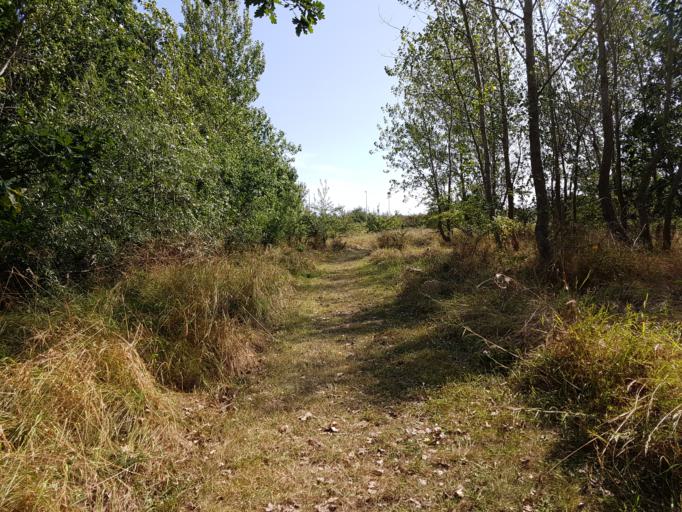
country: DK
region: Zealand
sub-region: Guldborgsund Kommune
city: Nykobing Falster
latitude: 54.5792
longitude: 11.9226
